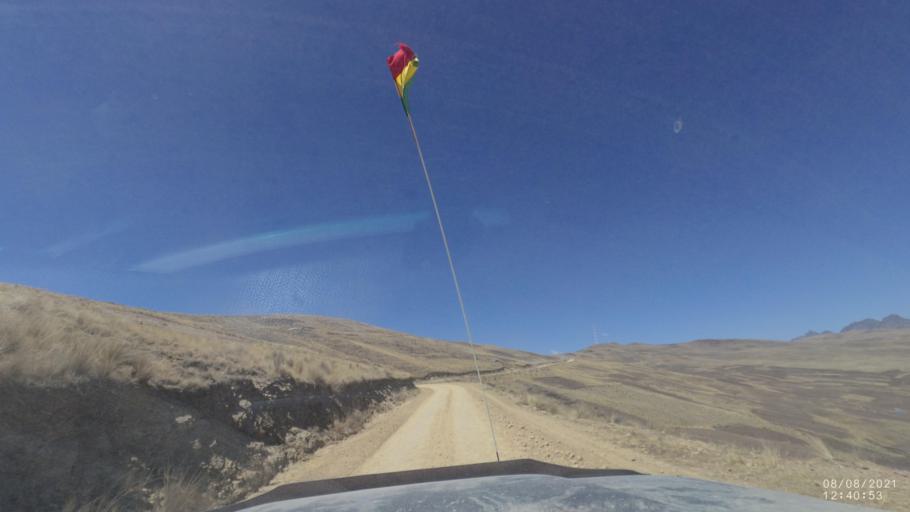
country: BO
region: Cochabamba
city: Colchani
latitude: -16.8311
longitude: -66.6221
